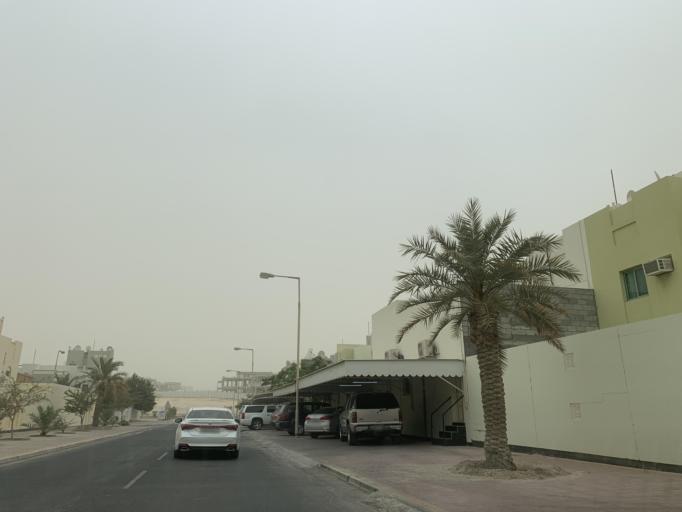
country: BH
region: Central Governorate
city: Madinat Hamad
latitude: 26.1347
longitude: 50.5131
